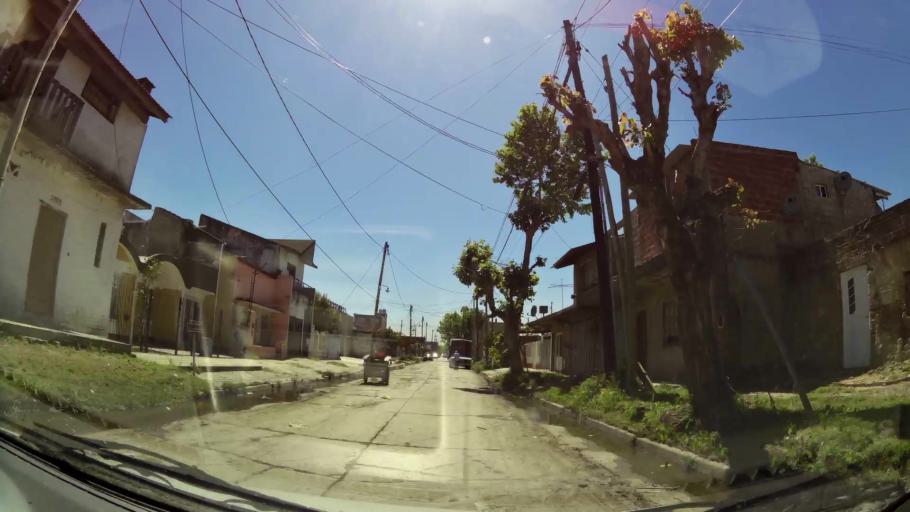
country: AR
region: Buenos Aires
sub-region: Partido de Quilmes
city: Quilmes
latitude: -34.7300
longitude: -58.3087
